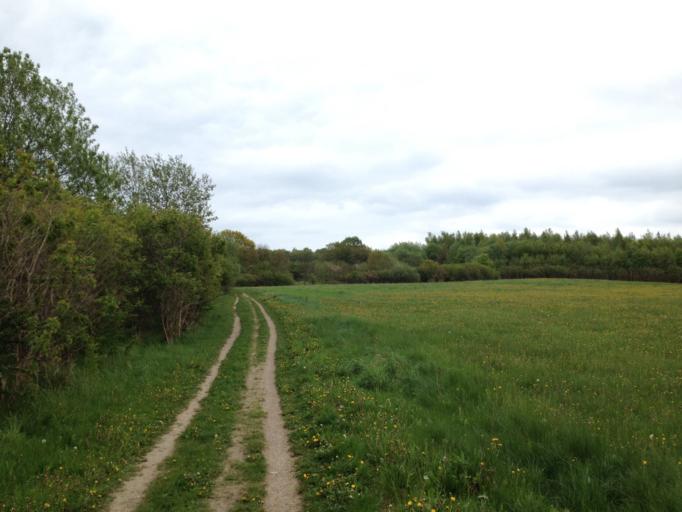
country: DK
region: Capital Region
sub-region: Fredensborg Kommune
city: Niva
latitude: 55.9491
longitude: 12.5057
